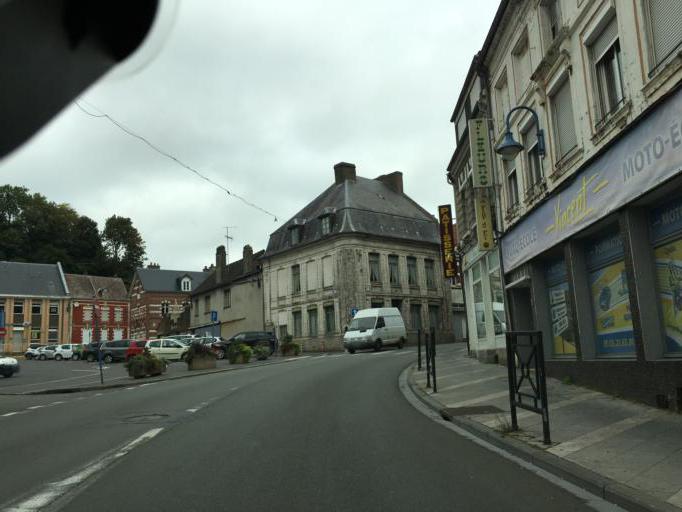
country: FR
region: Nord-Pas-de-Calais
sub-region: Departement du Pas-de-Calais
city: Saint-Pol-sur-Ternoise
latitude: 50.3826
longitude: 2.3369
